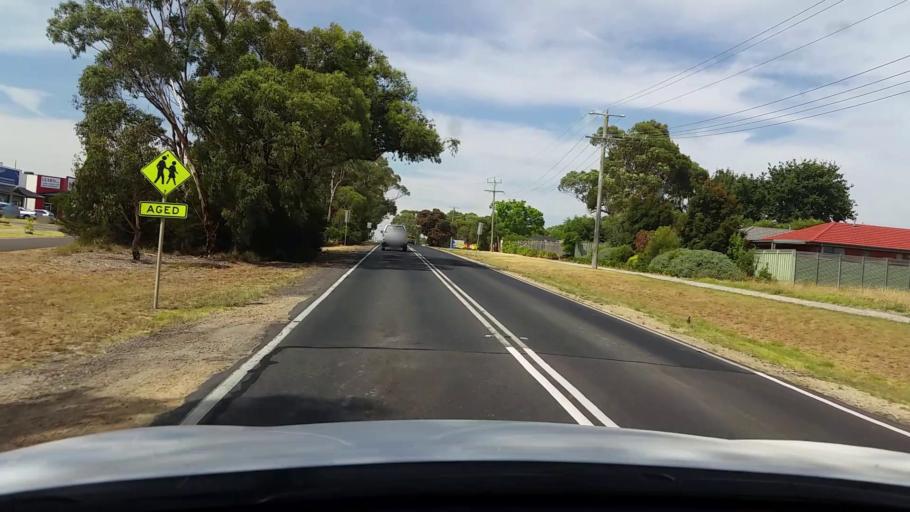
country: AU
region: Victoria
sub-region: Mornington Peninsula
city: Hastings
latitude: -38.3011
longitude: 145.1837
